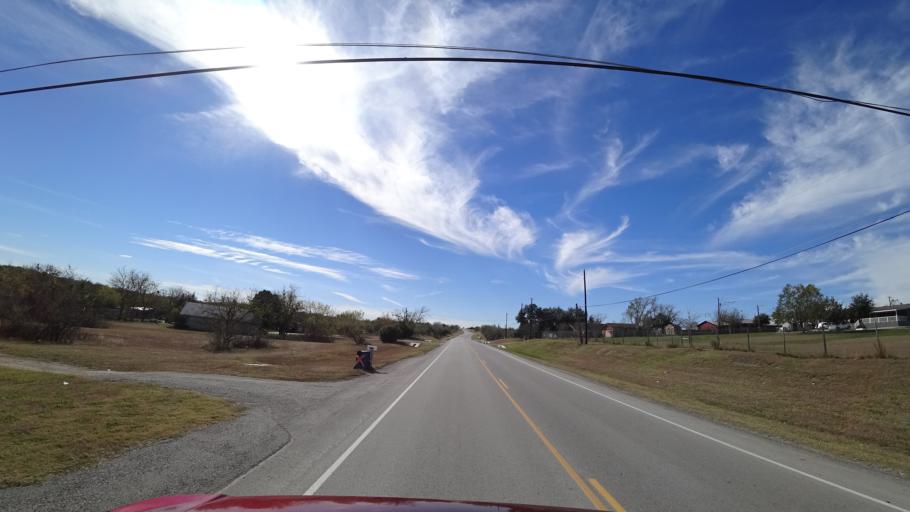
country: US
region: Texas
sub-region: Travis County
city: Onion Creek
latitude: 30.1250
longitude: -97.6870
